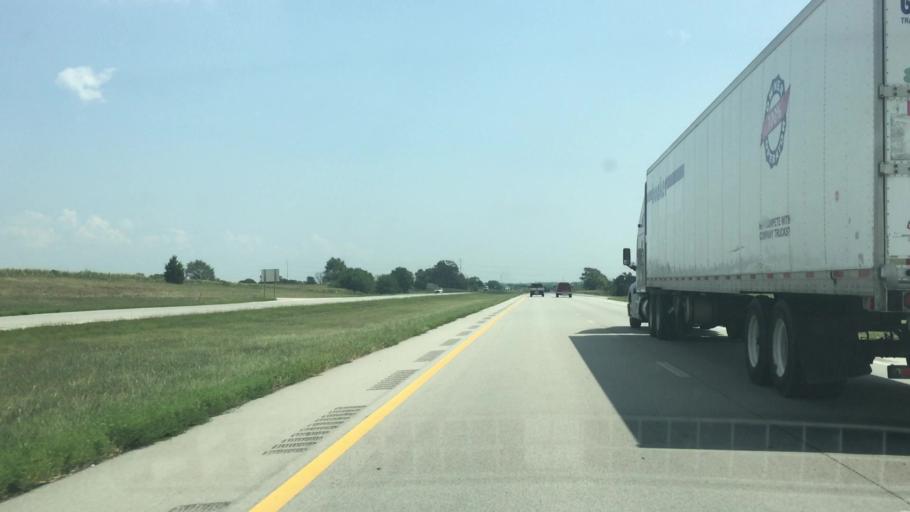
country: US
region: Kansas
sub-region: Johnson County
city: Edgerton
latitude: 38.7468
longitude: -94.9989
